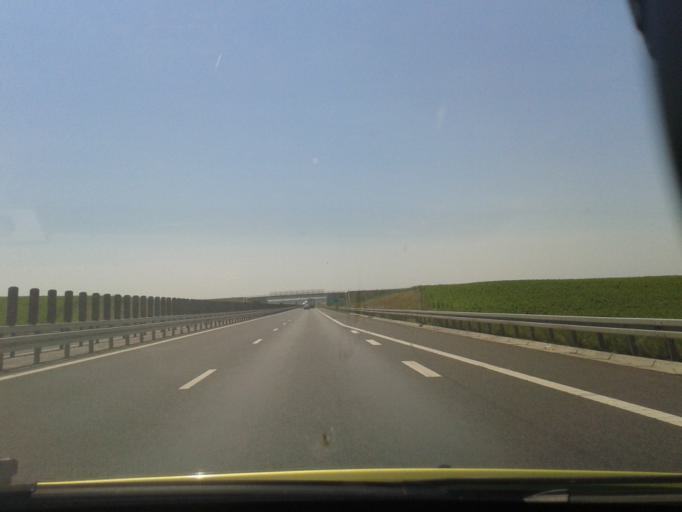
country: RO
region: Timis
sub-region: Comuna Giarmata
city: Giarmata
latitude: 45.8340
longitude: 21.3575
